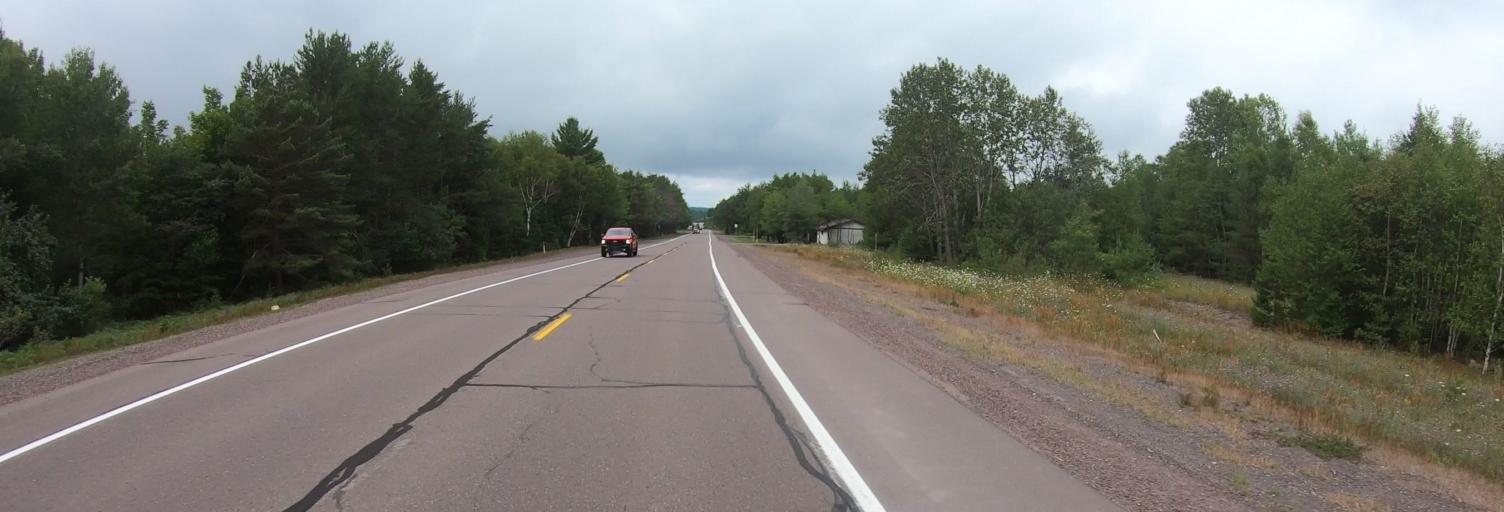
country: US
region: Michigan
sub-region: Houghton County
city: Laurium
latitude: 47.3004
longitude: -88.3781
